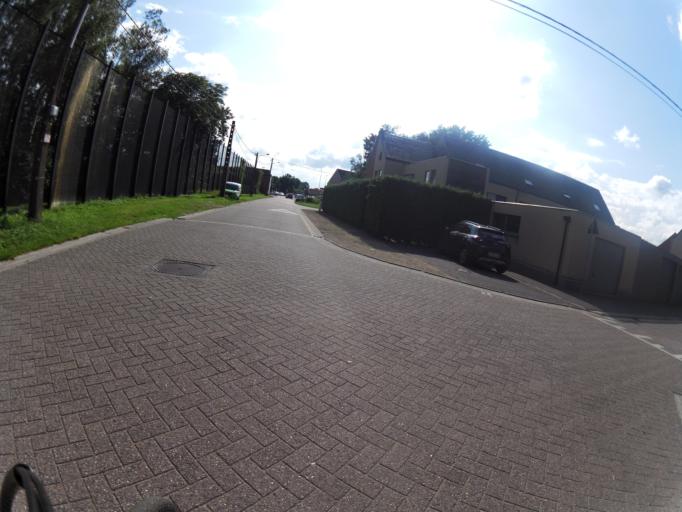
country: BE
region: Flanders
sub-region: Provincie Antwerpen
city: Mol
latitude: 51.1795
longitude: 5.1279
